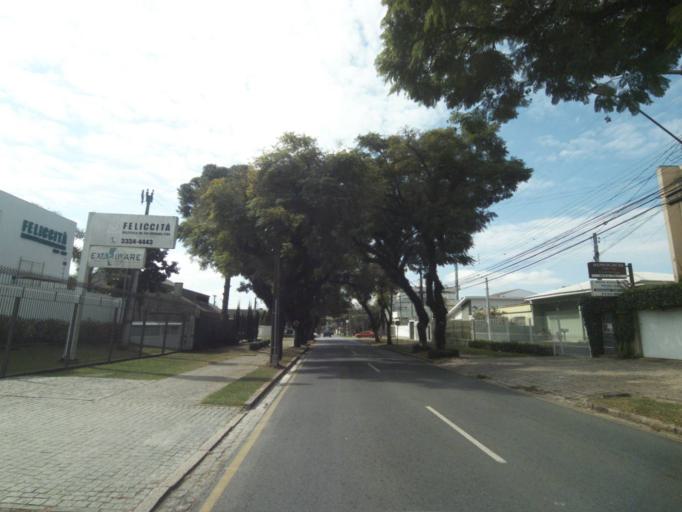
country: BR
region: Parana
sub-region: Curitiba
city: Curitiba
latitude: -25.4533
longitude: -49.2688
